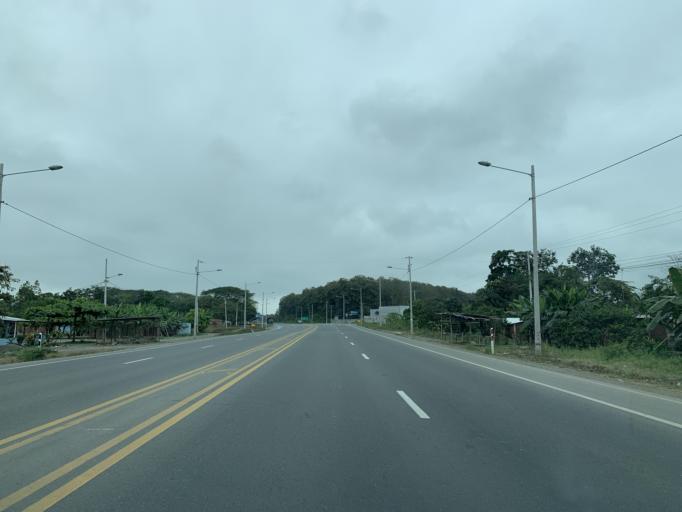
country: EC
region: Guayas
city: Coronel Marcelino Mariduena
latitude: -2.3225
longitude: -79.4590
